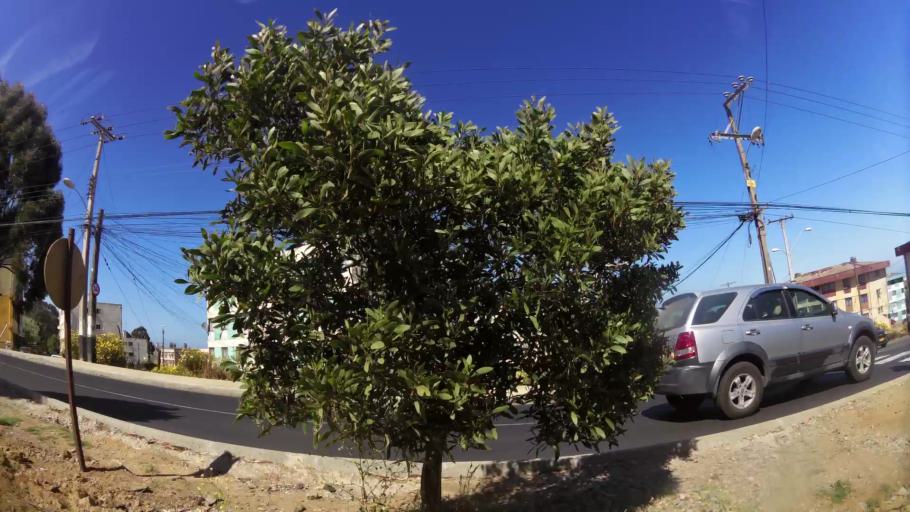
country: CL
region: Valparaiso
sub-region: Provincia de Valparaiso
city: Valparaiso
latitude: -33.0495
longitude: -71.6511
